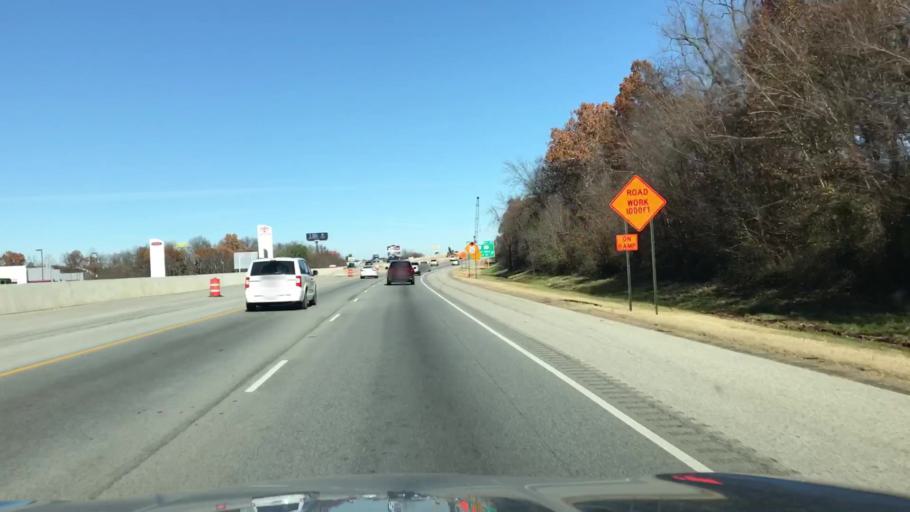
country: US
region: Arkansas
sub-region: Benton County
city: Bentonville
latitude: 36.3295
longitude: -94.1845
